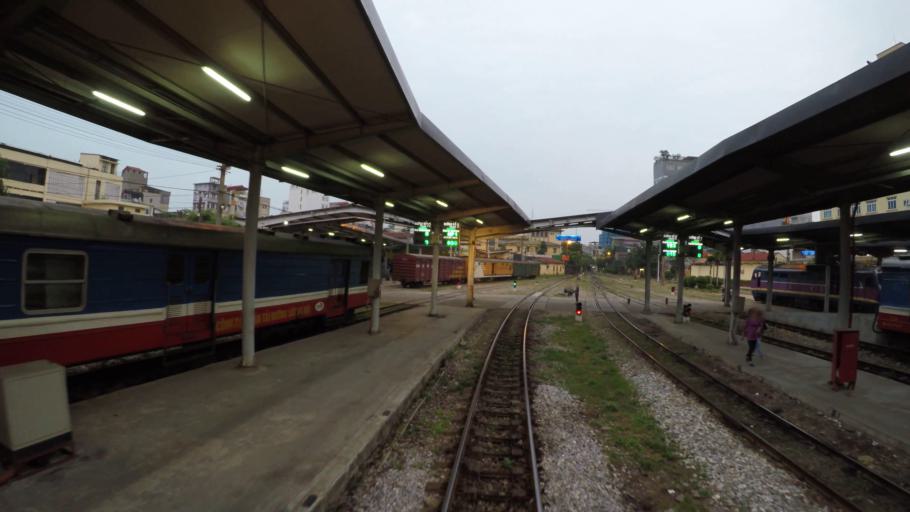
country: VN
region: Ha Noi
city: Hanoi
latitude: 21.0283
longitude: 105.8418
